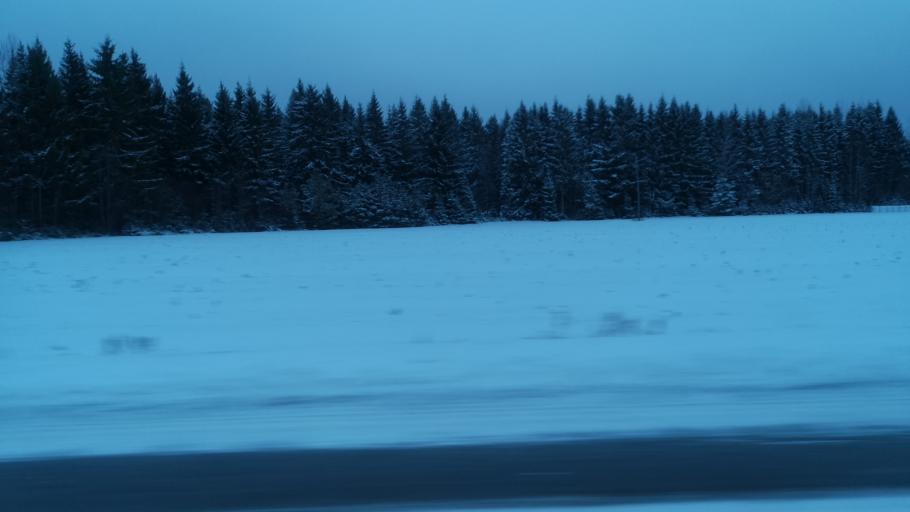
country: FI
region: Southern Savonia
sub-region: Savonlinna
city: Savonlinna
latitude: 61.8976
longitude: 28.9235
